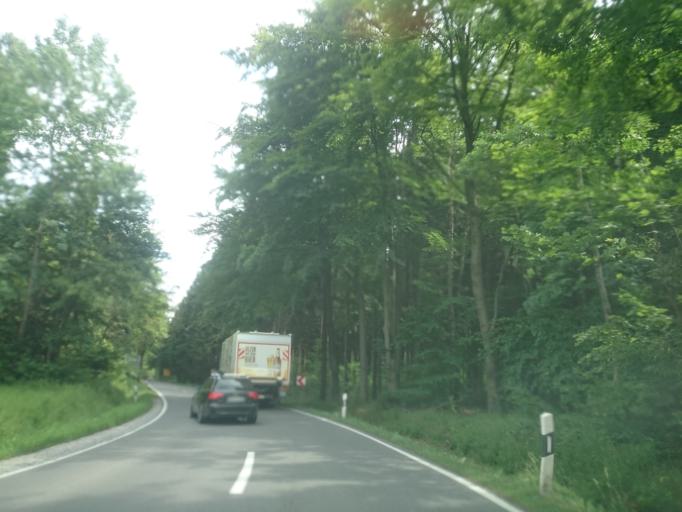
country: DE
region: Saxony
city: Augustusburg
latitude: 50.7907
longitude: 13.1106
